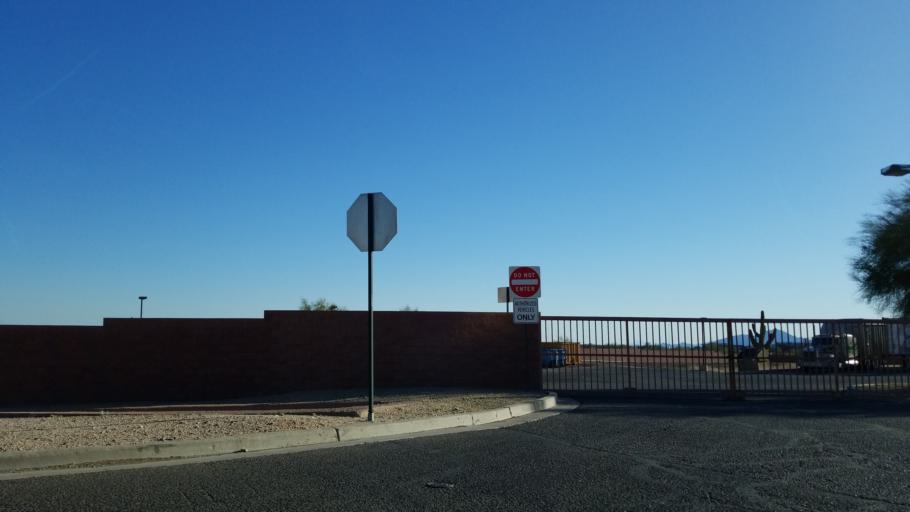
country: US
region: Arizona
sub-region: Maricopa County
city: Paradise Valley
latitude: 33.6552
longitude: -111.8950
